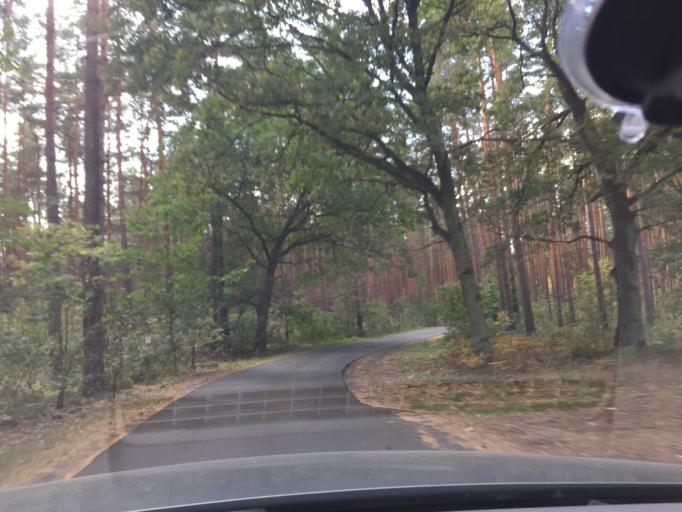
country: DE
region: Brandenburg
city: Spreenhagen
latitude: 52.3739
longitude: 13.8951
